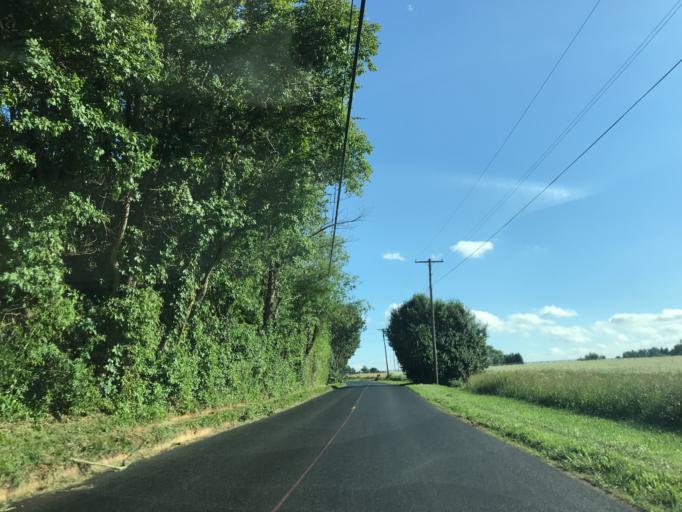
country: US
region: Maryland
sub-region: Carroll County
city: Hampstead
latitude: 39.6324
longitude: -76.8180
